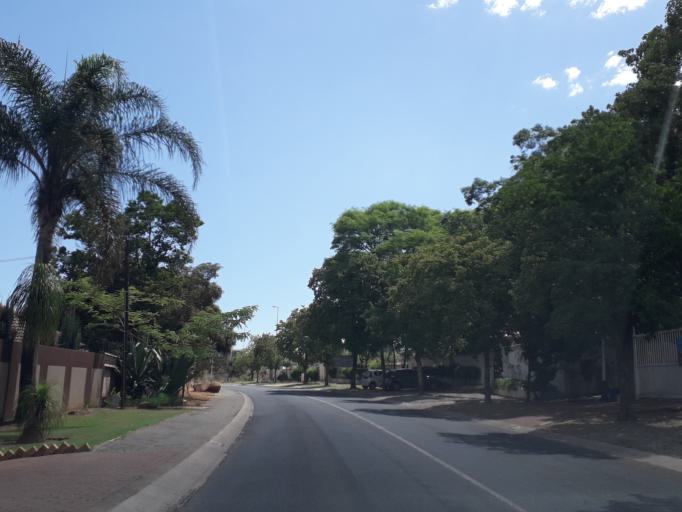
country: ZA
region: Gauteng
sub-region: City of Johannesburg Metropolitan Municipality
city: Roodepoort
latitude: -26.1129
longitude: 27.9577
